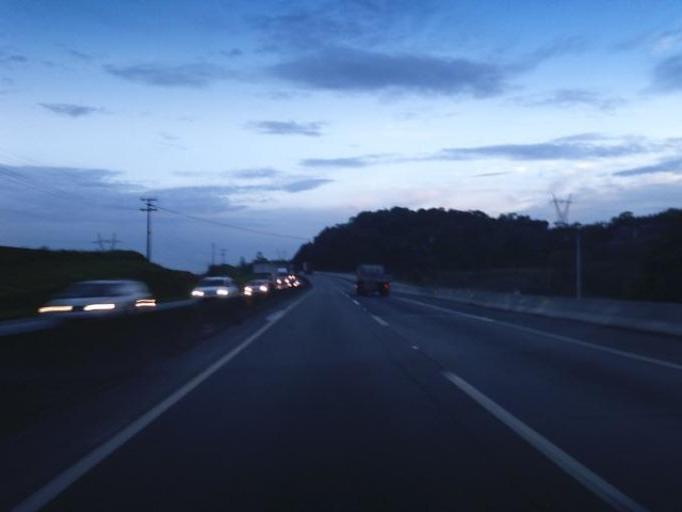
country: BR
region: Santa Catarina
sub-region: Joinville
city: Joinville
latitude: -26.2740
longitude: -48.8940
